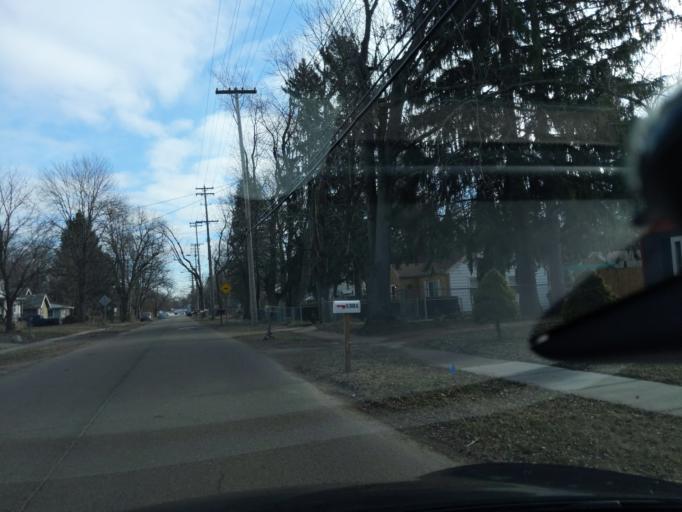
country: US
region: Michigan
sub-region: Ingham County
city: Lansing
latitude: 42.6929
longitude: -84.5707
